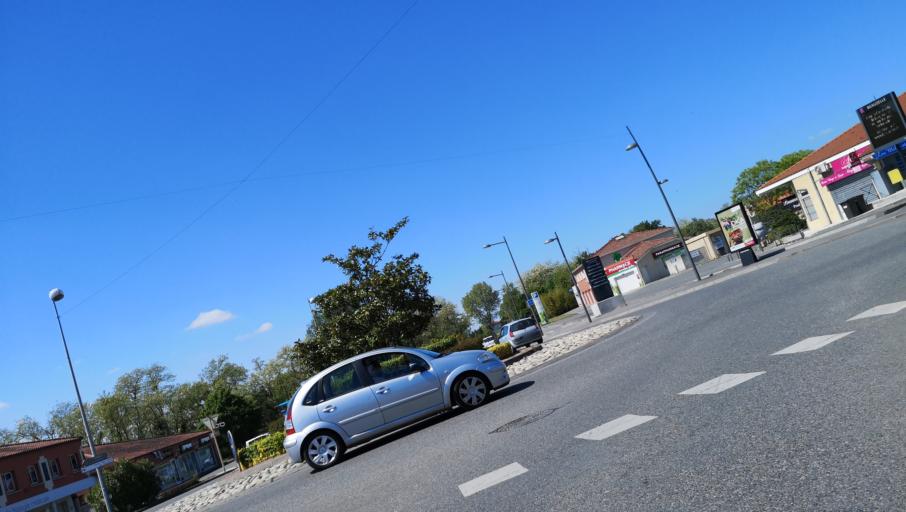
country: FR
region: Midi-Pyrenees
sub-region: Departement de la Haute-Garonne
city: Beauzelle
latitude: 43.6698
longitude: 1.3682
